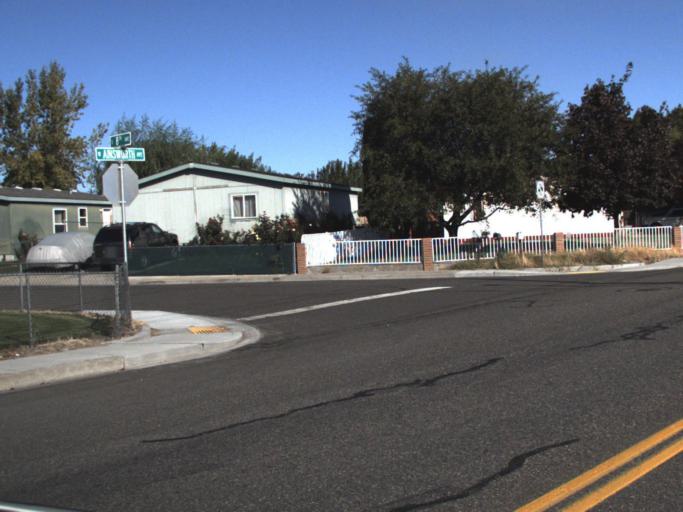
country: US
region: Washington
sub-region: Franklin County
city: Pasco
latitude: 46.2235
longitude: -119.0990
